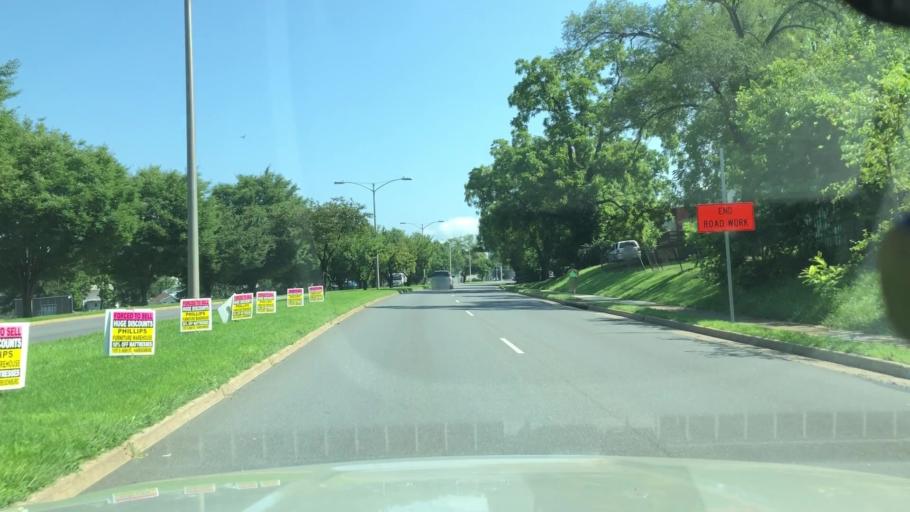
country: US
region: Virginia
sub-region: City of Harrisonburg
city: Harrisonburg
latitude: 38.4459
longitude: -78.8760
